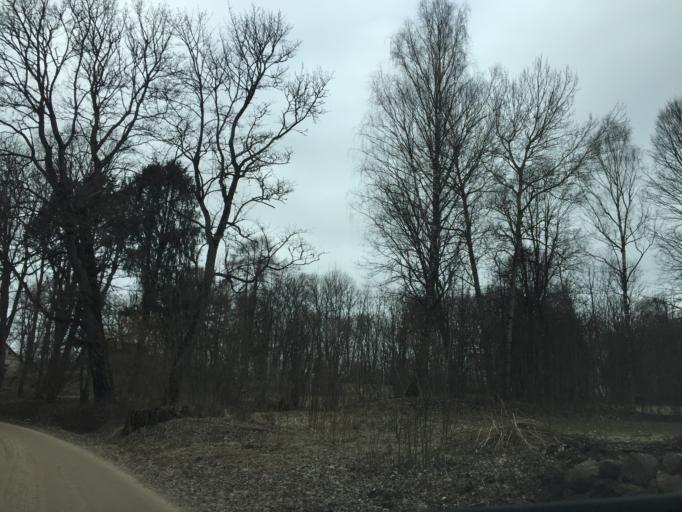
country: LV
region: Kraslavas Rajons
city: Kraslava
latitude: 55.9779
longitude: 27.1733
